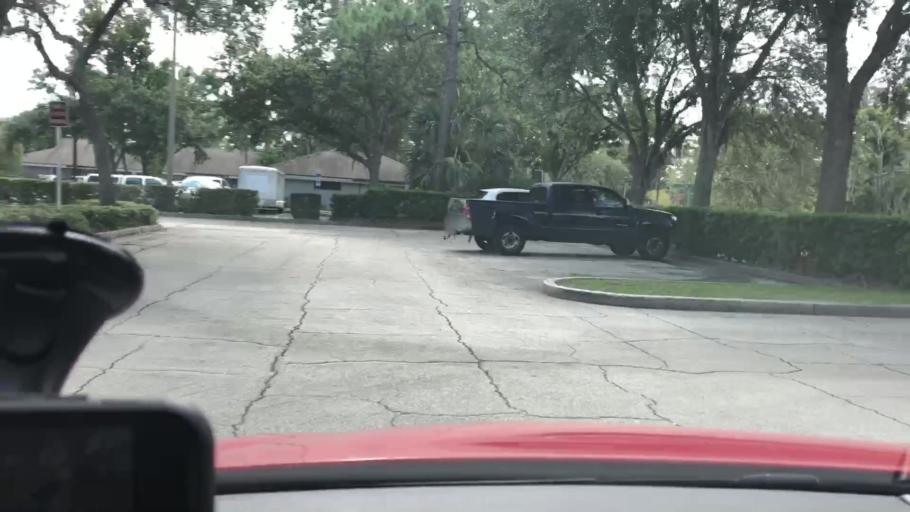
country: US
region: Florida
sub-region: Volusia County
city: Port Orange
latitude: 29.1262
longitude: -81.0104
